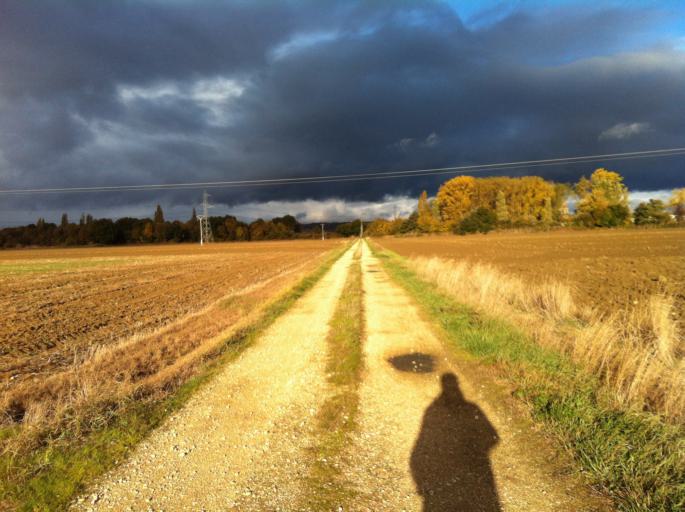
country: ES
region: Basque Country
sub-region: Provincia de Alava
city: Gasteiz / Vitoria
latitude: 42.8614
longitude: -2.7238
